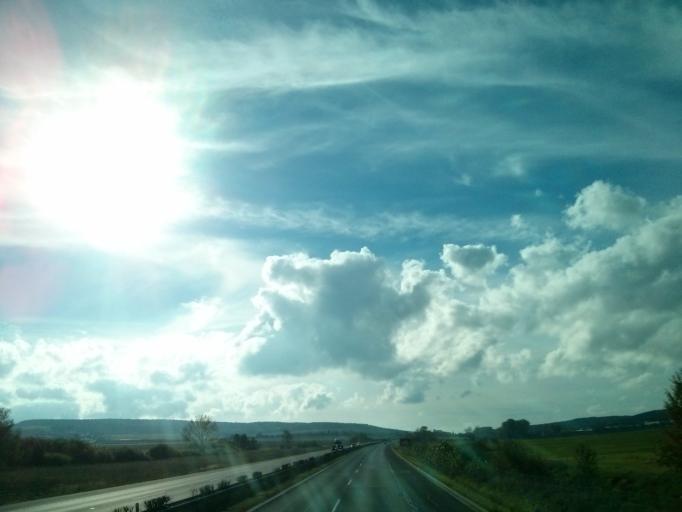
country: CZ
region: Central Bohemia
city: Komarov
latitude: 49.8486
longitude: 13.8552
